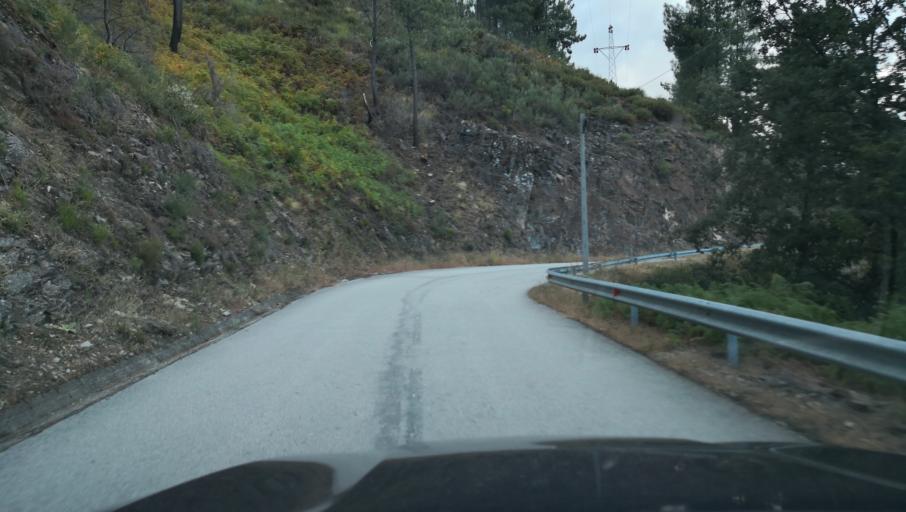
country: PT
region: Vila Real
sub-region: Santa Marta de Penaguiao
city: Santa Marta de Penaguiao
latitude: 41.2551
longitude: -7.8569
